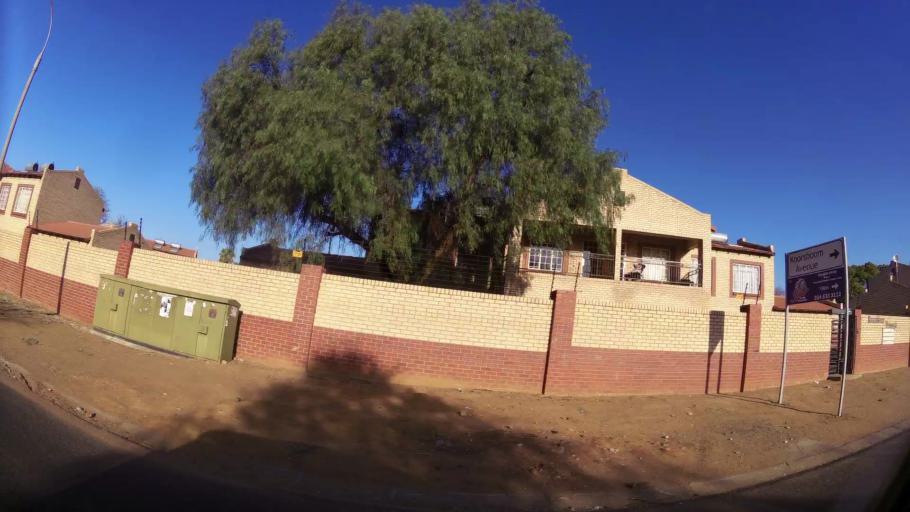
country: ZA
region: North-West
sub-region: Bojanala Platinum District Municipality
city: Rustenburg
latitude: -25.6842
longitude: 27.2164
